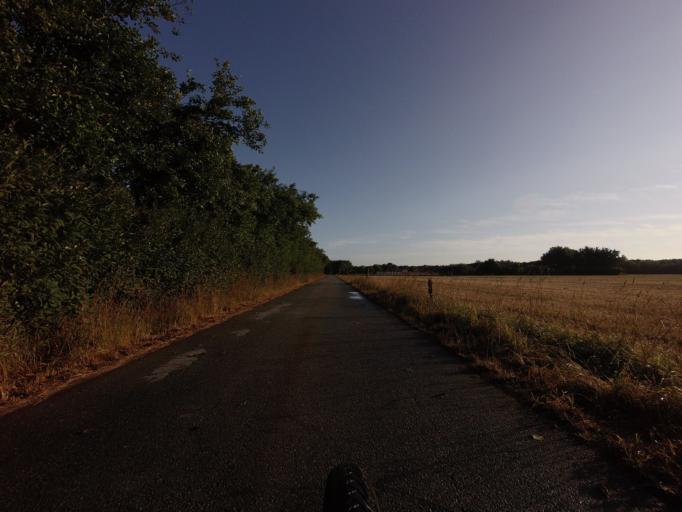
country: DK
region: North Denmark
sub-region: Hjorring Kommune
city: Vra
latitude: 57.3606
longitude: 9.8659
